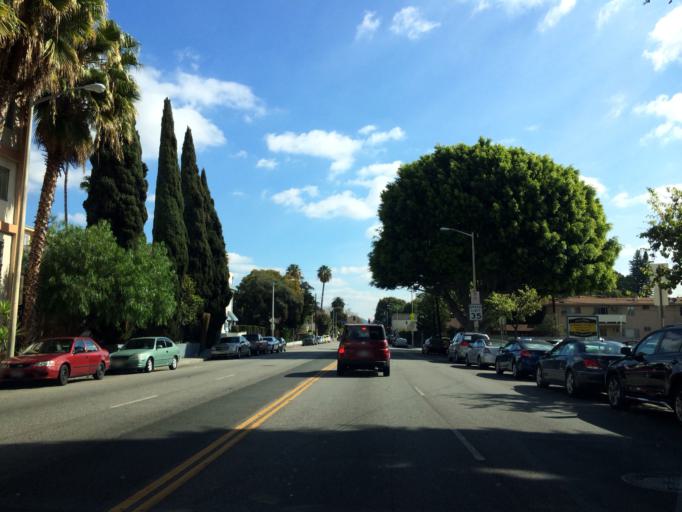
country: US
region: California
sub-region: Los Angeles County
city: West Hollywood
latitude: 34.0944
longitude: -118.3515
